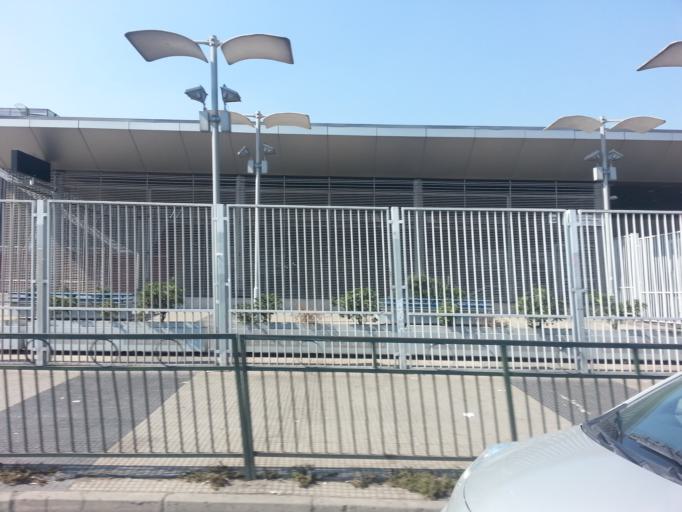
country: CL
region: Santiago Metropolitan
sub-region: Provincia de Santiago
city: La Pintana
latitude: -33.5383
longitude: -70.6644
